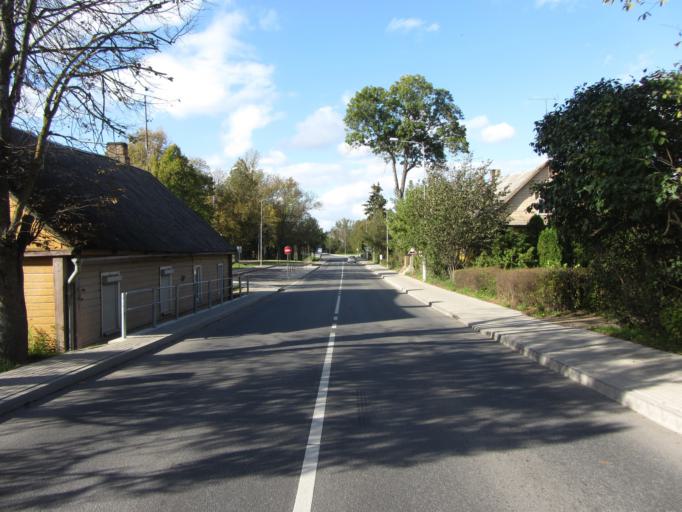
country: LT
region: Panevezys
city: Rokiskis
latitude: 55.9416
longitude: 25.7947
